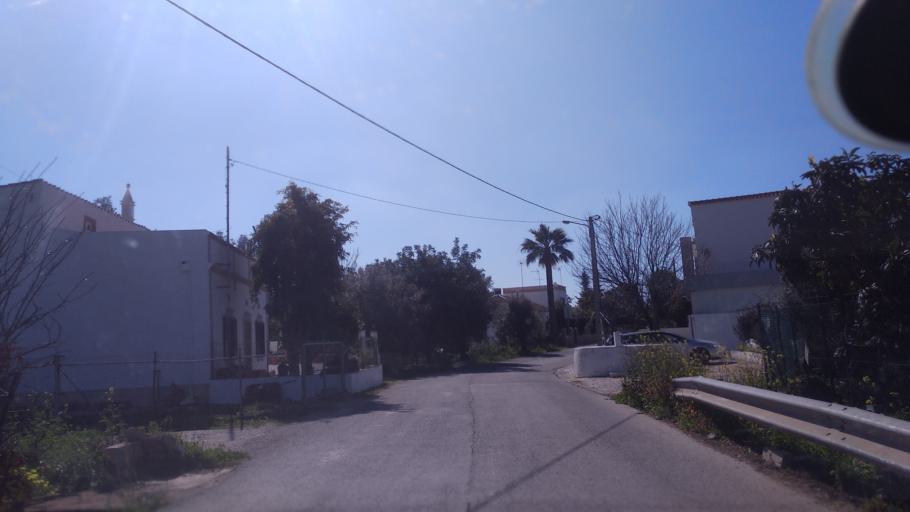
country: PT
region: Faro
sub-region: Sao Bras de Alportel
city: Sao Bras de Alportel
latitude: 37.1260
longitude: -7.9213
